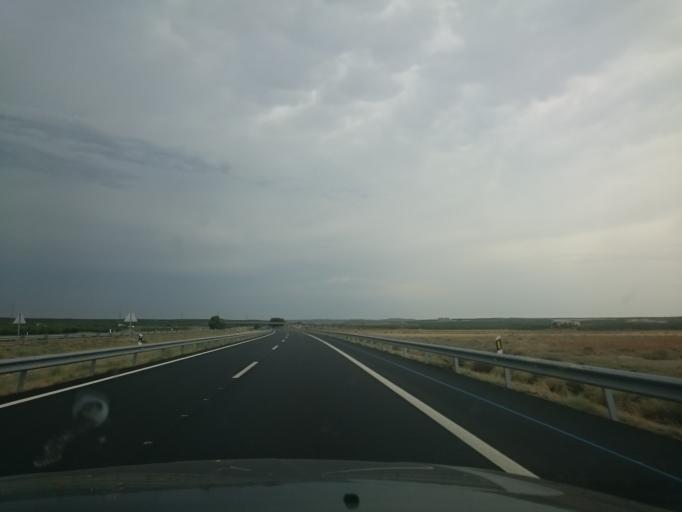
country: ES
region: Aragon
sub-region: Provincia de Zaragoza
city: Pina de Ebro
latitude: 41.5355
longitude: -0.5176
